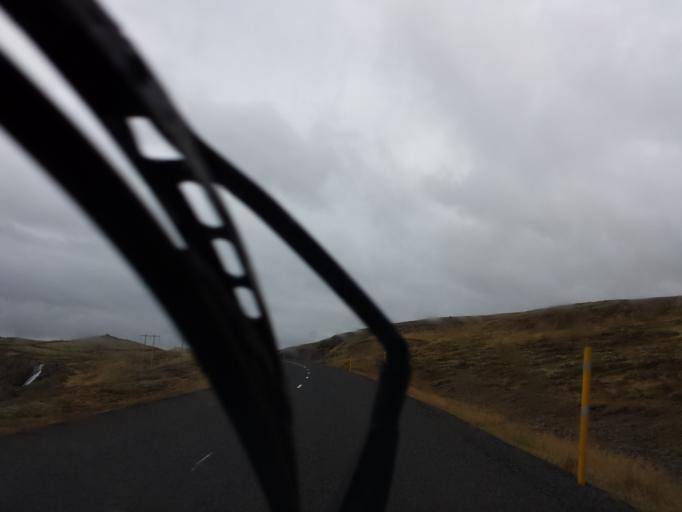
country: IS
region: West
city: Stykkisholmur
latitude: 64.9028
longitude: -22.8498
